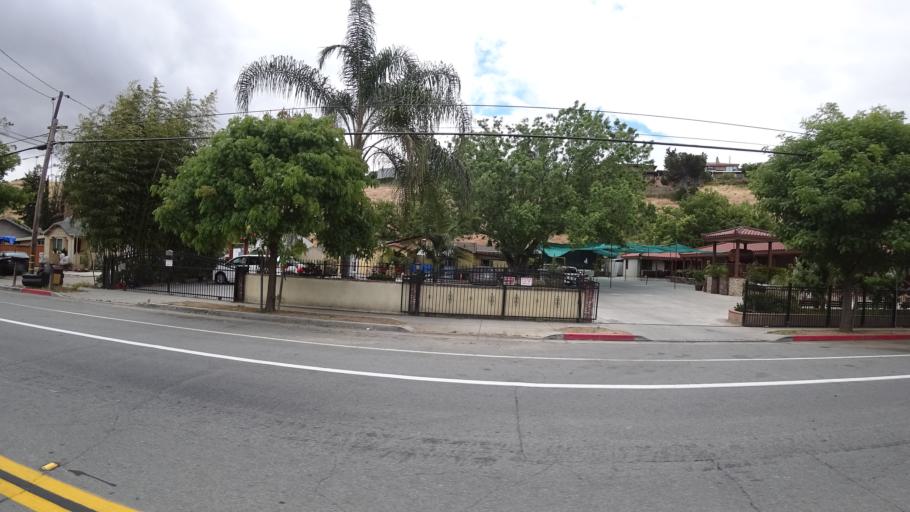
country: US
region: California
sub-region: Santa Clara County
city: Seven Trees
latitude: 37.2781
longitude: -121.8283
